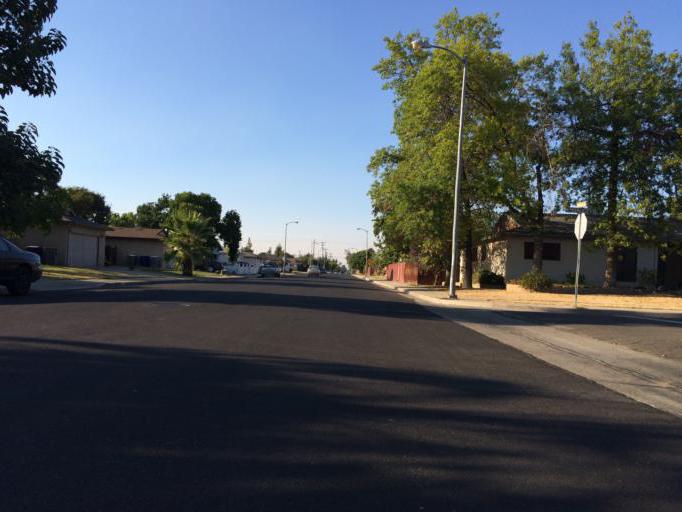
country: US
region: California
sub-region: Fresno County
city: Tarpey Village
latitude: 36.7988
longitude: -119.7136
